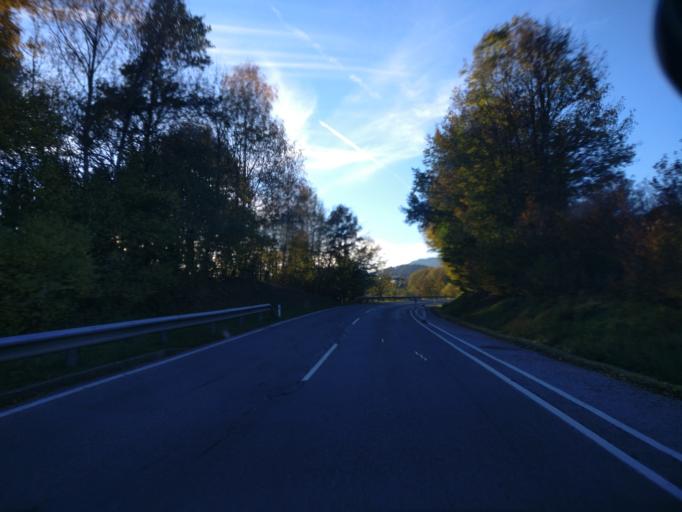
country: AT
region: Salzburg
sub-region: Politischer Bezirk Sankt Johann im Pongau
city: Schwarzach im Pongau
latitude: 47.3248
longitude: 13.1643
